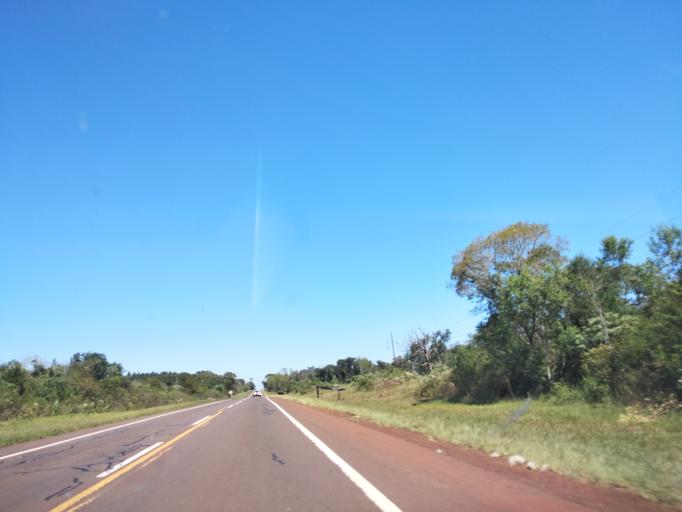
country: AR
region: Misiones
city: Puerto Libertad
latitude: -25.7671
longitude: -54.5383
